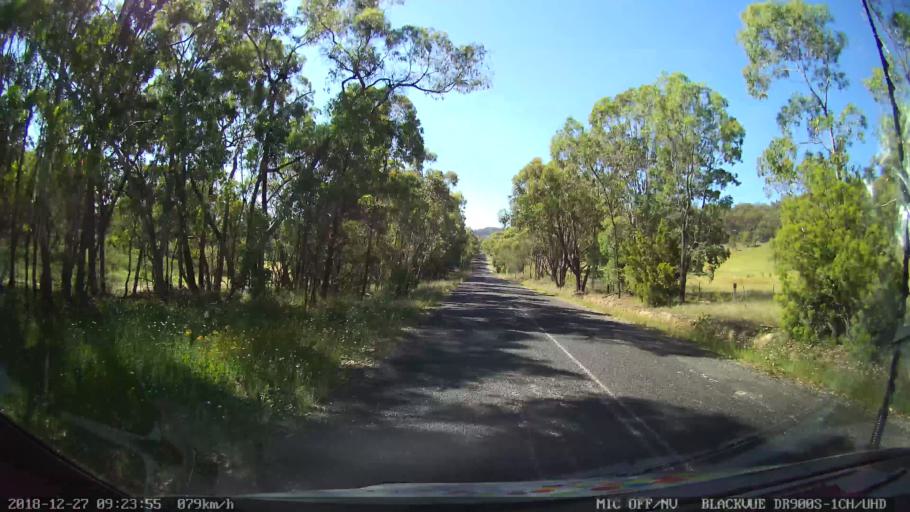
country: AU
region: New South Wales
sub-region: Lithgow
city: Portland
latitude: -33.1310
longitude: 149.9962
